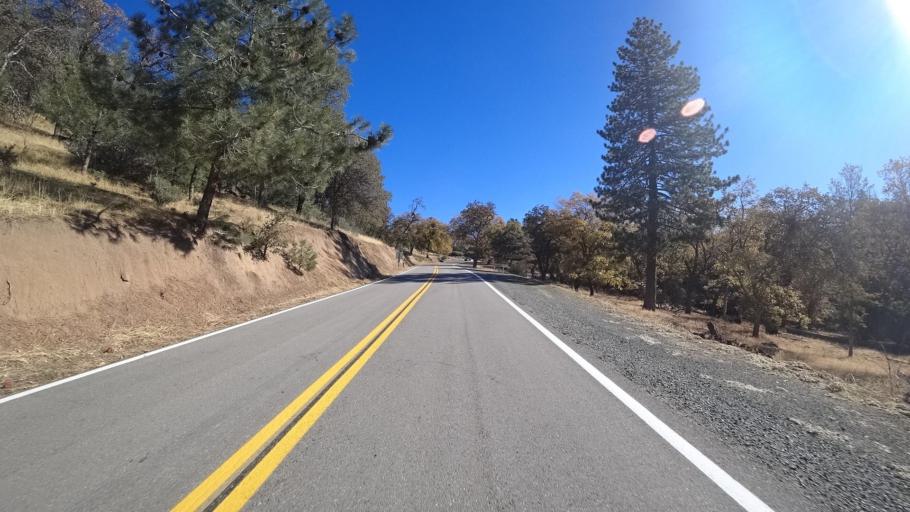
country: US
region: California
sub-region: Kern County
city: Alta Sierra
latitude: 35.7374
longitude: -118.6150
